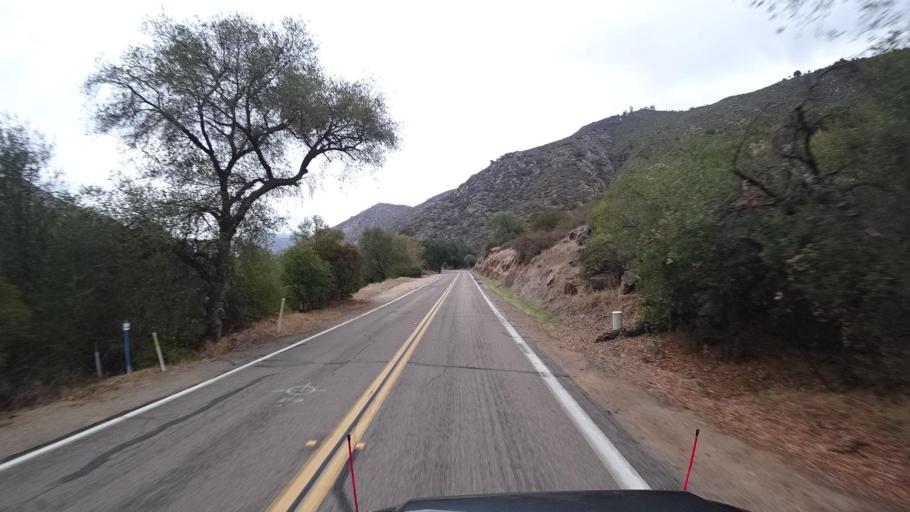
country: US
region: California
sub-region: San Diego County
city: Harbison Canyon
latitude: 32.8870
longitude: -116.8292
